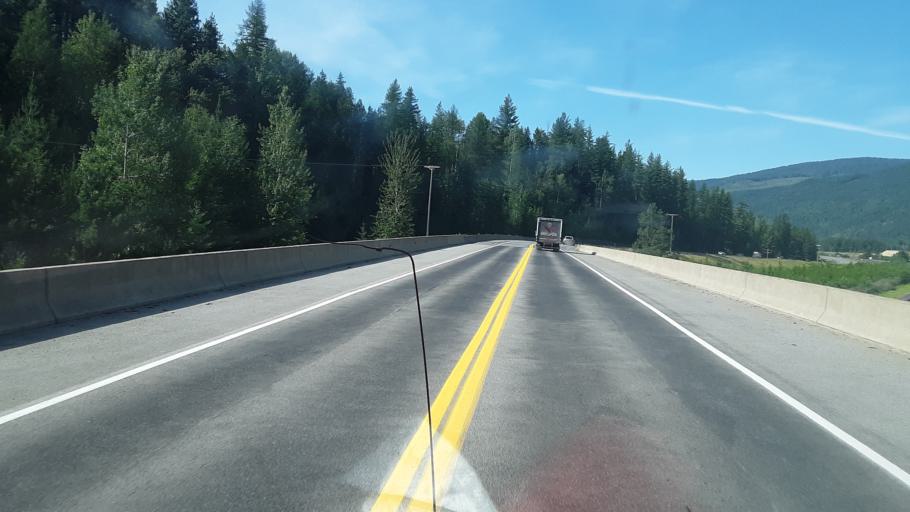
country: US
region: Idaho
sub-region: Bonner County
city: Ponderay
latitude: 48.4134
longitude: -116.5171
